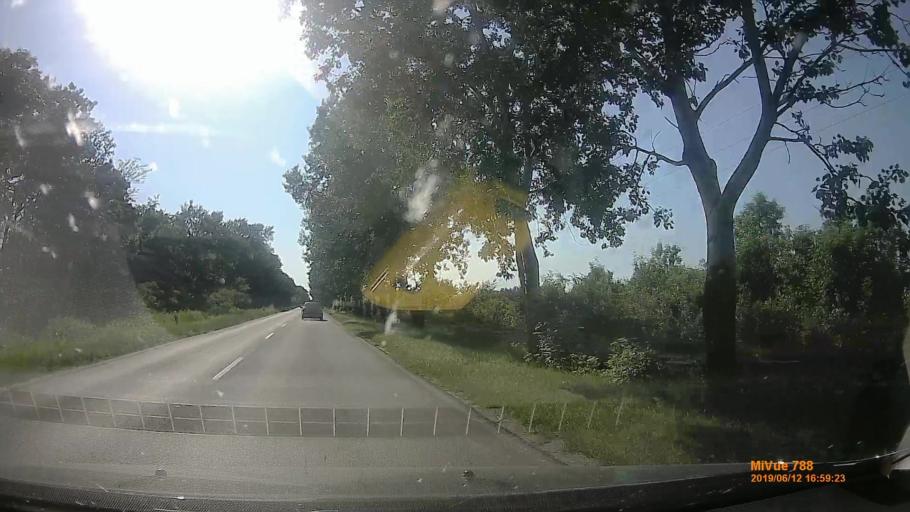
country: HU
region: Csongrad
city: Deszk
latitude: 46.2181
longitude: 20.2668
